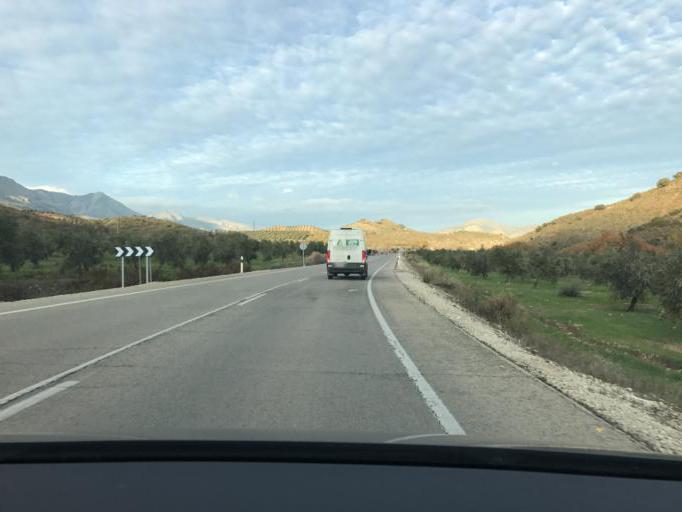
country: ES
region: Andalusia
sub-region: Provincia de Jaen
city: Huelma
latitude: 37.6638
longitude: -3.4175
